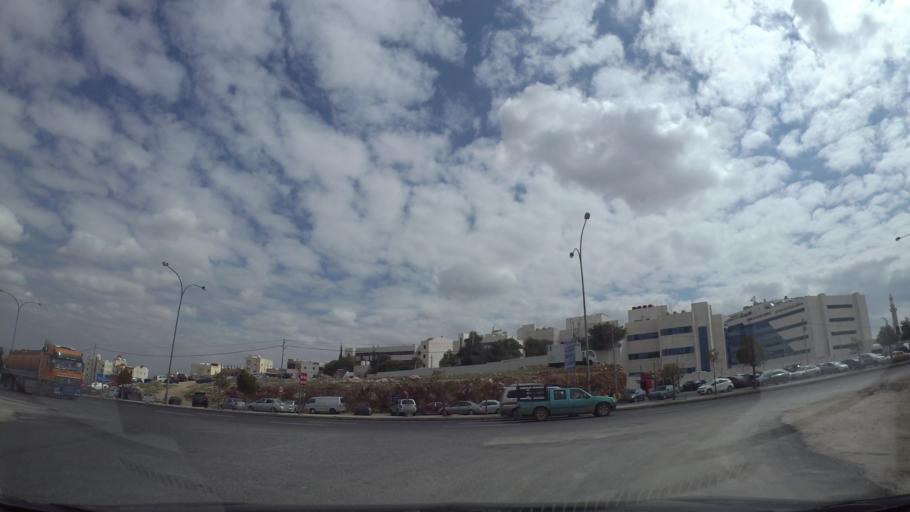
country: JO
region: Amman
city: Amman
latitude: 32.0017
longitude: 35.9177
